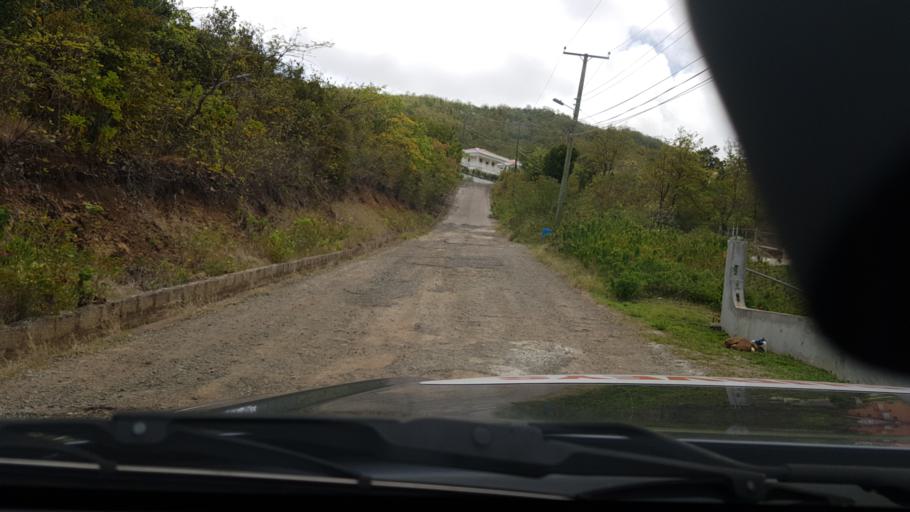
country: LC
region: Gros-Islet
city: Gros Islet
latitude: 14.0676
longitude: -60.9313
